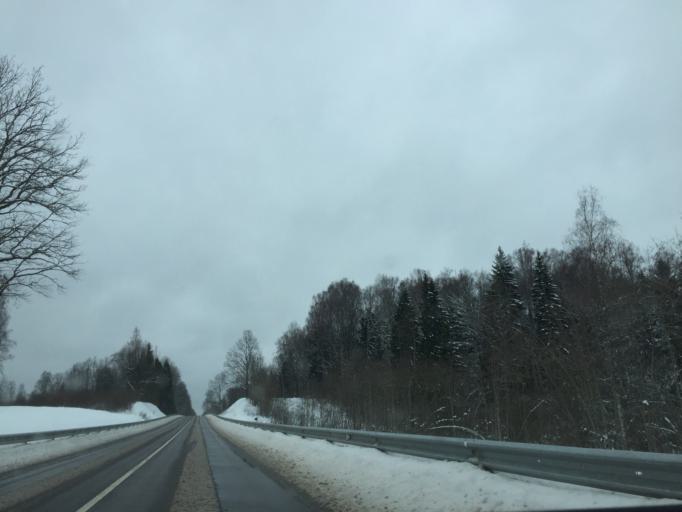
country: LV
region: Ligatne
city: Ligatne
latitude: 57.1316
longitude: 25.0864
